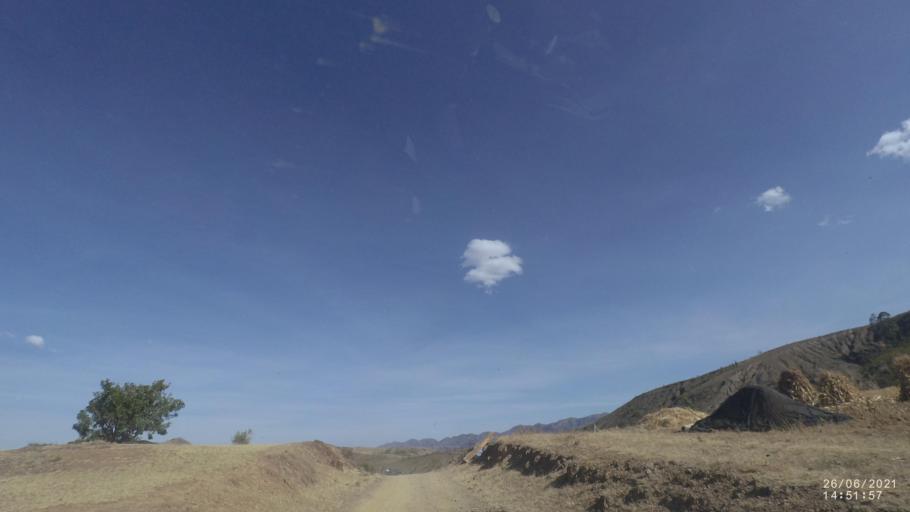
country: BO
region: Cochabamba
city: Mizque
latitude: -17.9250
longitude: -65.6272
